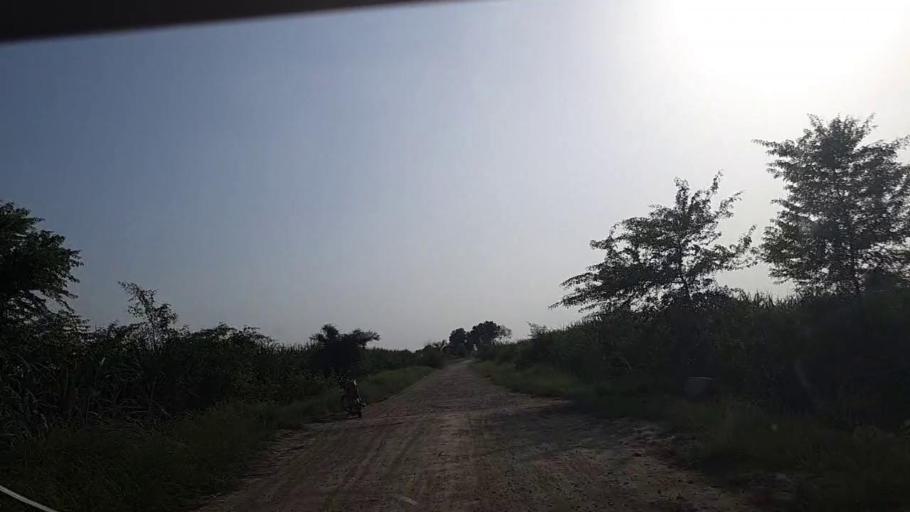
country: PK
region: Sindh
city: Ghotki
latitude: 27.9884
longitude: 69.2603
